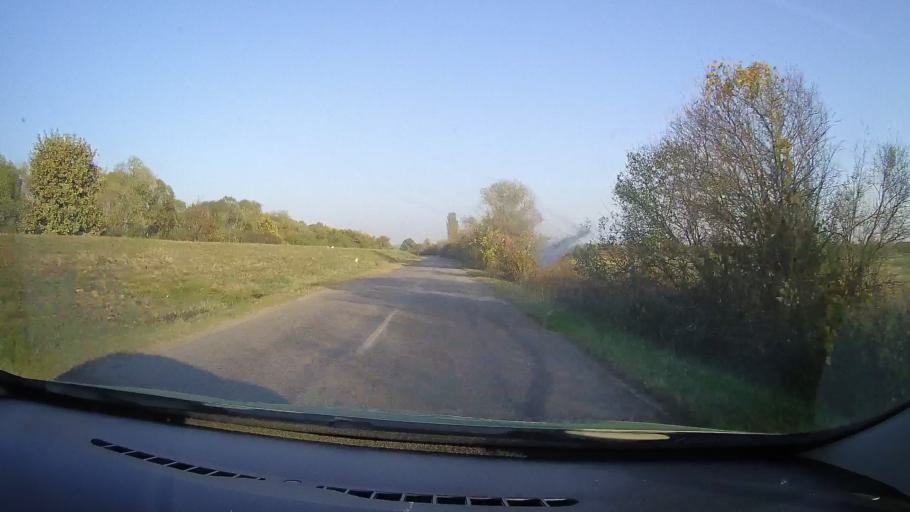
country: RO
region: Arad
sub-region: Comuna Silindia
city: Silindia
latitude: 46.3365
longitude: 21.8863
